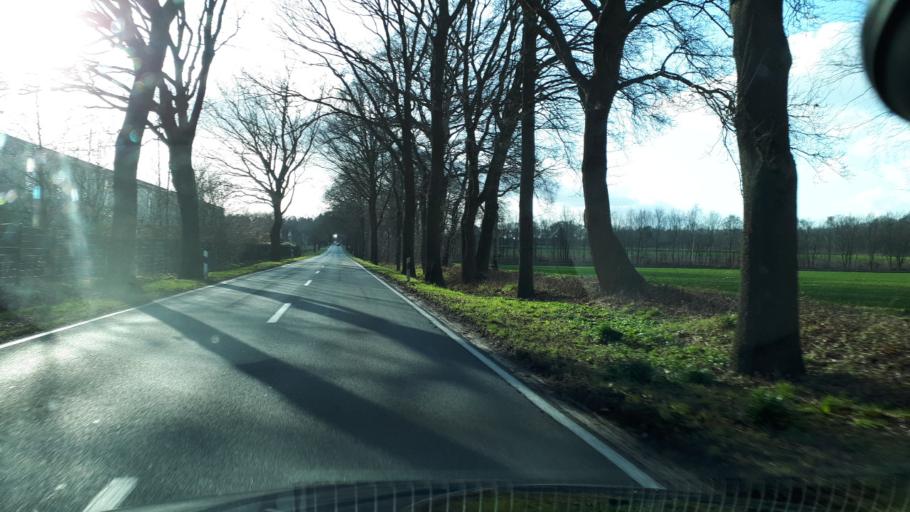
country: DE
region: Lower Saxony
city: Molbergen
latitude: 52.8552
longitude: 7.9463
